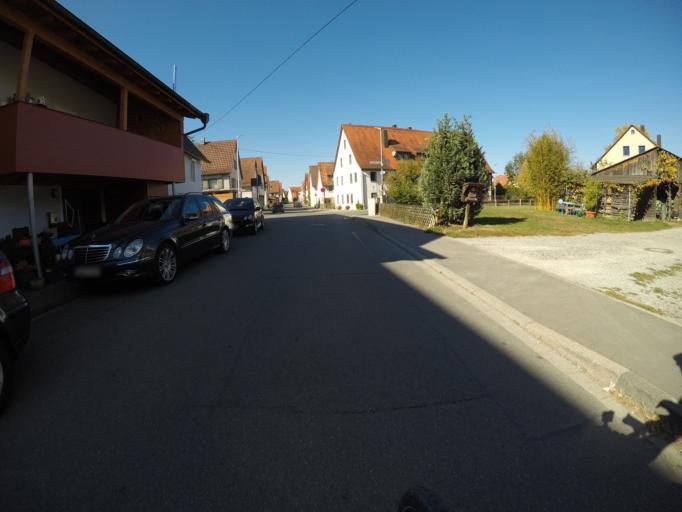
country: DE
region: Baden-Wuerttemberg
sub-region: Tuebingen Region
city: Rottenburg
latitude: 48.5256
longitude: 8.9646
